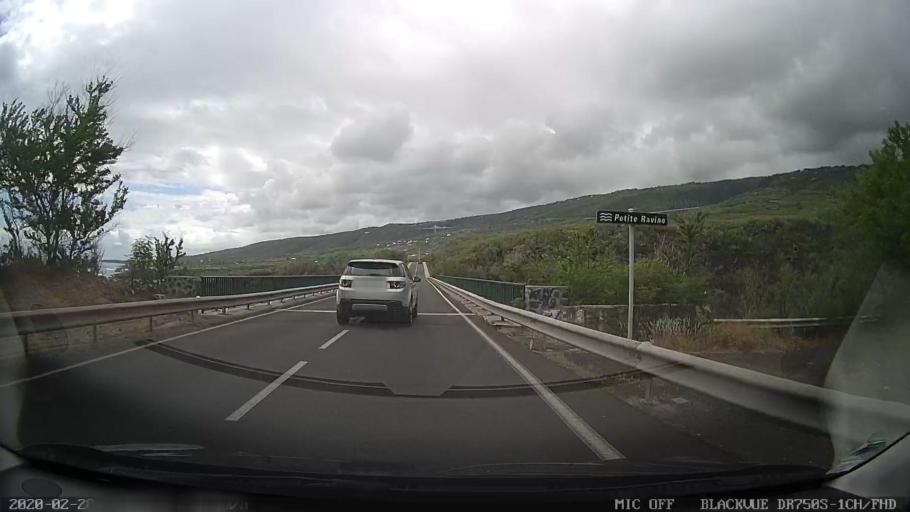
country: RE
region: Reunion
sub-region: Reunion
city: Saint-Leu
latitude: -21.1355
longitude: 55.2725
